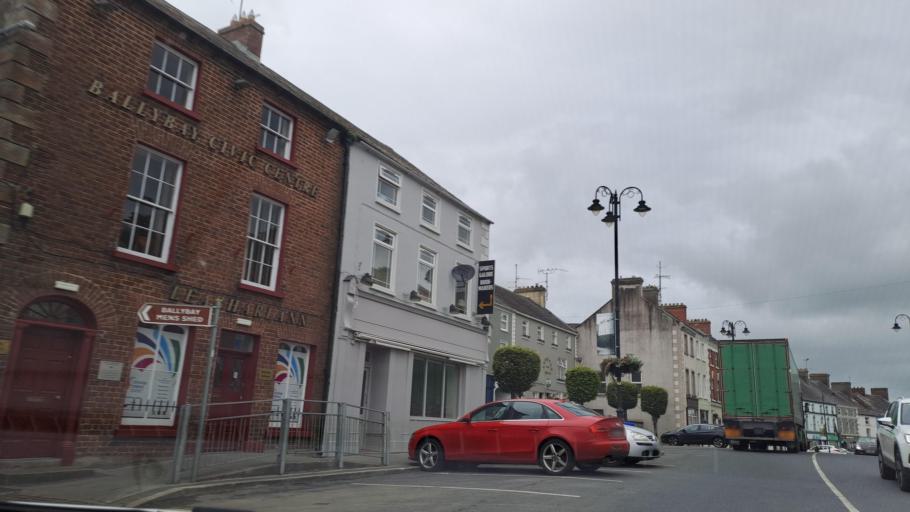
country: IE
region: Ulster
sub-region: County Monaghan
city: Monaghan
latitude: 54.1275
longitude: -6.9024
